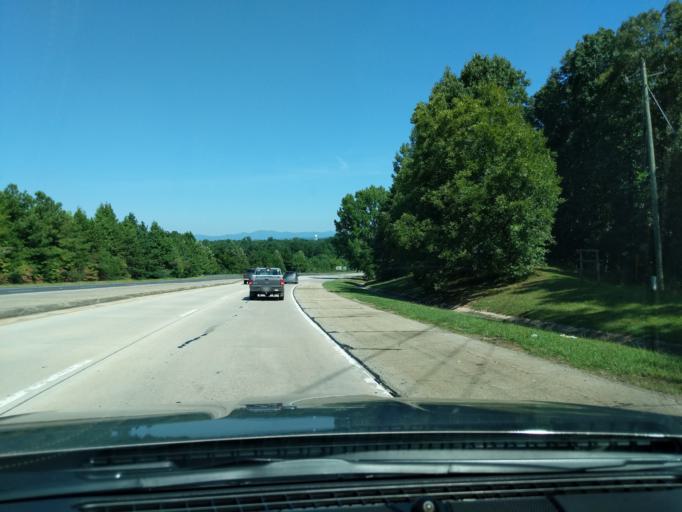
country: US
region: Georgia
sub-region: Habersham County
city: Baldwin
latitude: 34.5022
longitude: -83.5448
